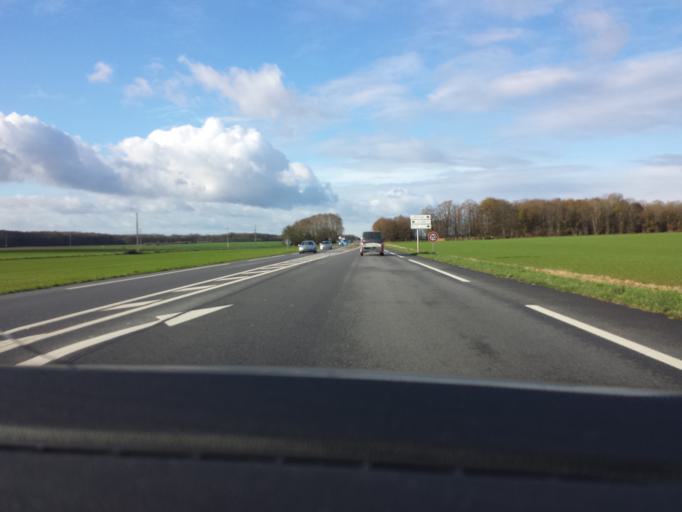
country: FR
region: Haute-Normandie
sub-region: Departement de l'Eure
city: Menilles
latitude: 49.0128
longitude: 1.2865
